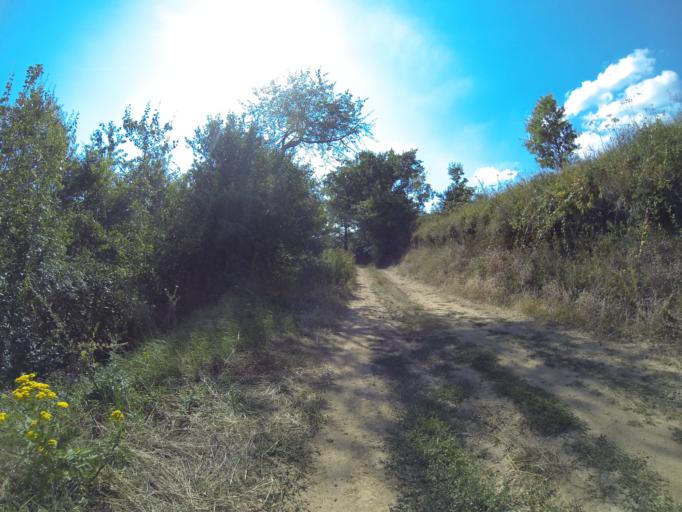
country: RO
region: Mehedinti
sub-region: Comuna Svinita
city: Svinita
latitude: 44.5610
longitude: 22.1574
